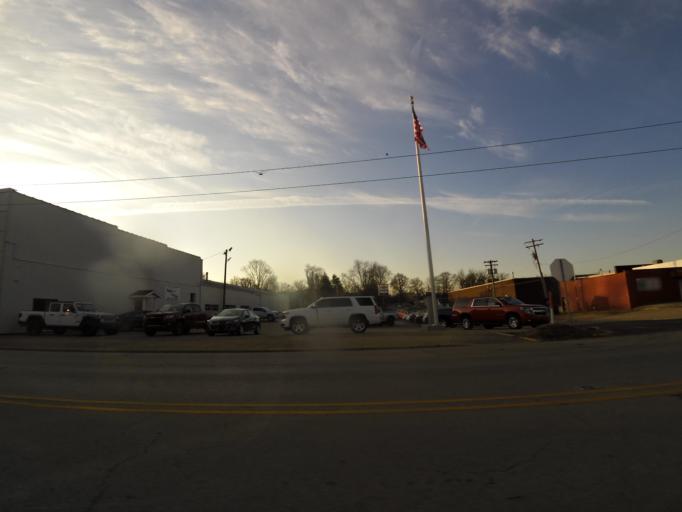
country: US
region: Illinois
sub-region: Fayette County
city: Vandalia
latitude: 38.9607
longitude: -89.0915
